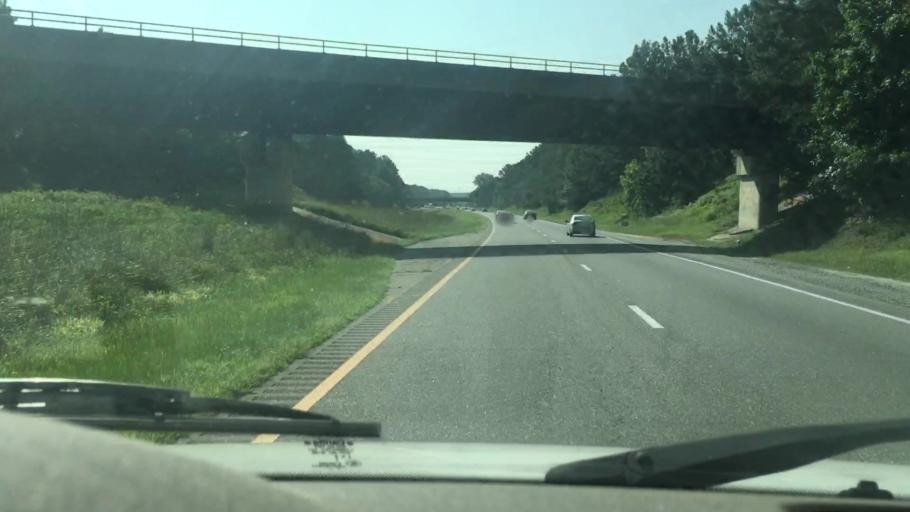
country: US
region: North Carolina
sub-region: Lincoln County
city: Lowesville
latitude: 35.3593
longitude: -80.9835
